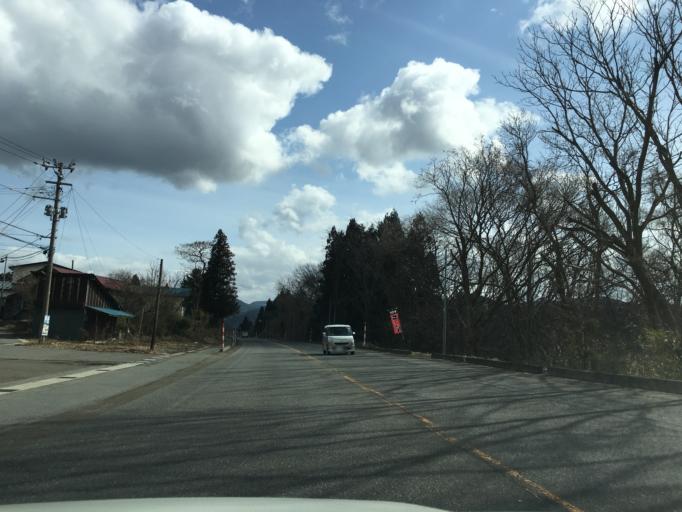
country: JP
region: Akita
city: Odate
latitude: 40.2252
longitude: 140.6018
